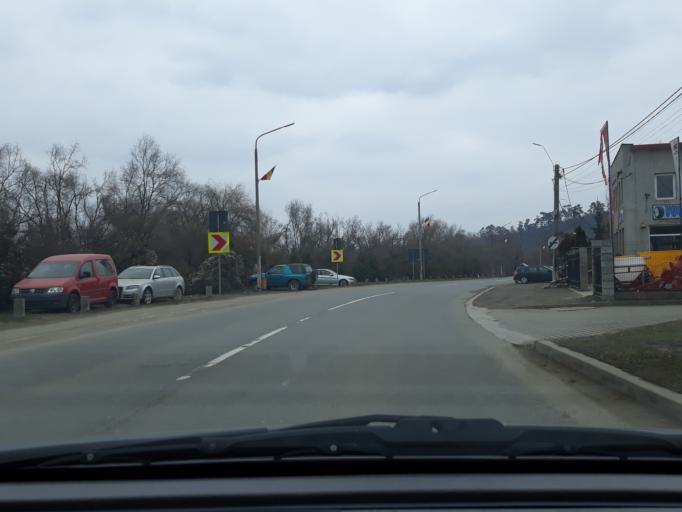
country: RO
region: Salaj
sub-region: Oras Simleu Silvaniei
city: Simleu Silvaniei
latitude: 47.2315
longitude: 22.7873
